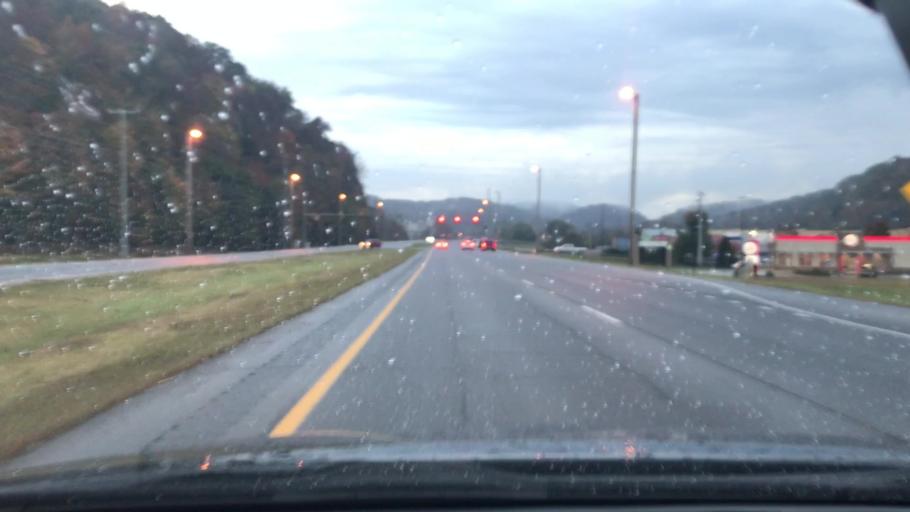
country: US
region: Tennessee
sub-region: Cheatham County
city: Ashland City
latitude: 36.2510
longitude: -87.0341
